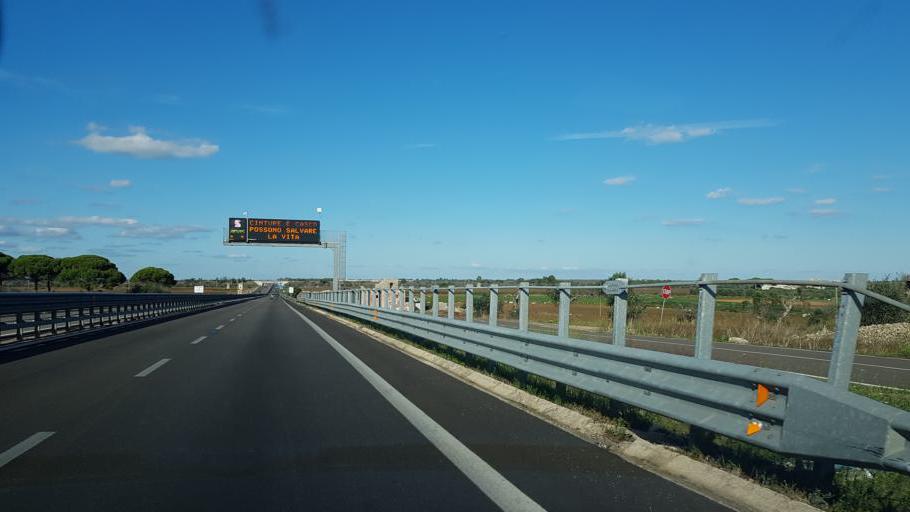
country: IT
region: Apulia
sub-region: Provincia di Lecce
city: Collemeto
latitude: 40.2477
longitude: 18.1144
